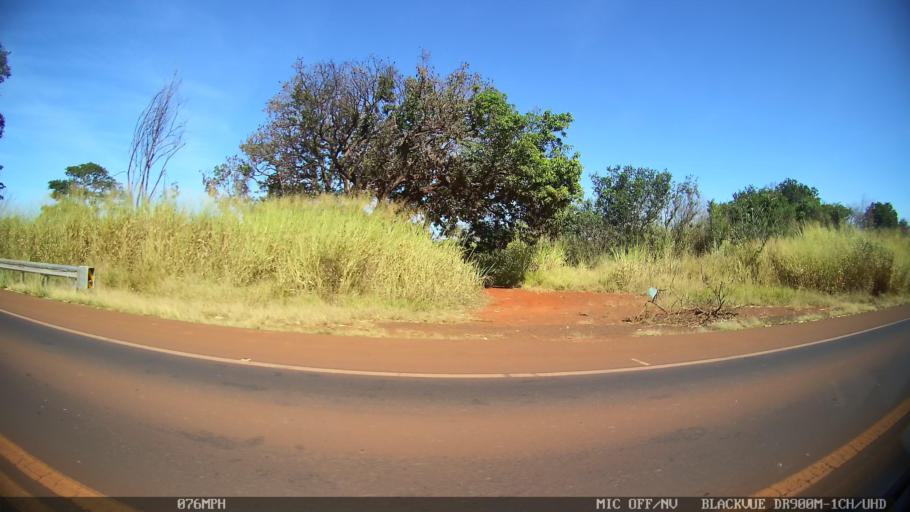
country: BR
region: Sao Paulo
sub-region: Sao Joaquim Da Barra
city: Sao Joaquim da Barra
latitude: -20.5414
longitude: -47.8044
